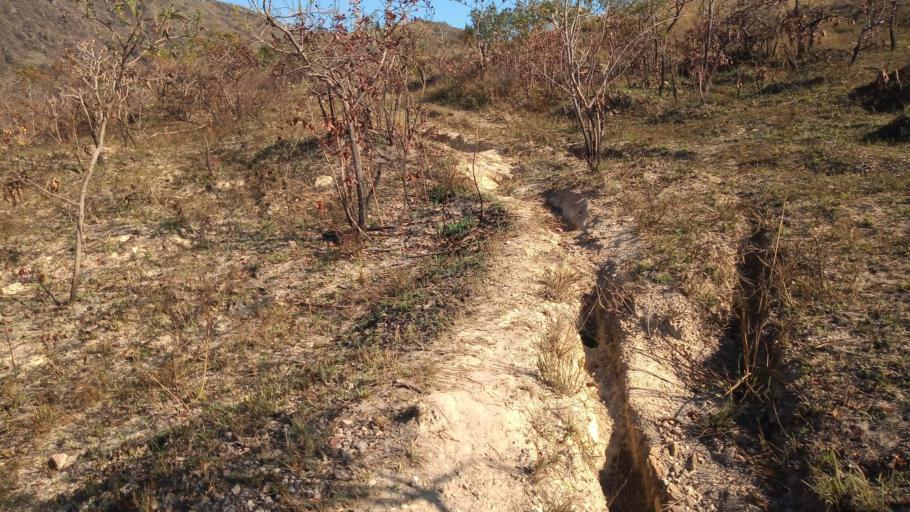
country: BR
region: Minas Gerais
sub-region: Sao Joao Del Rei
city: Sao Joao del Rei
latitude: -21.1288
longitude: -44.2702
